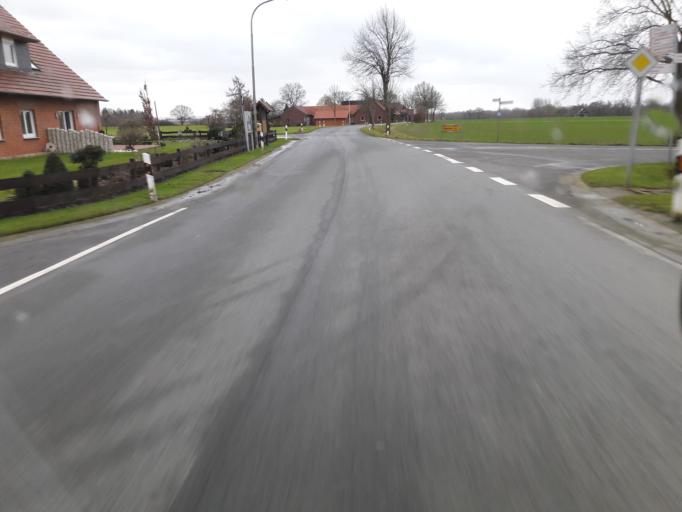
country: DE
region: Lower Saxony
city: Raddestorf
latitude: 52.4467
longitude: 8.9888
